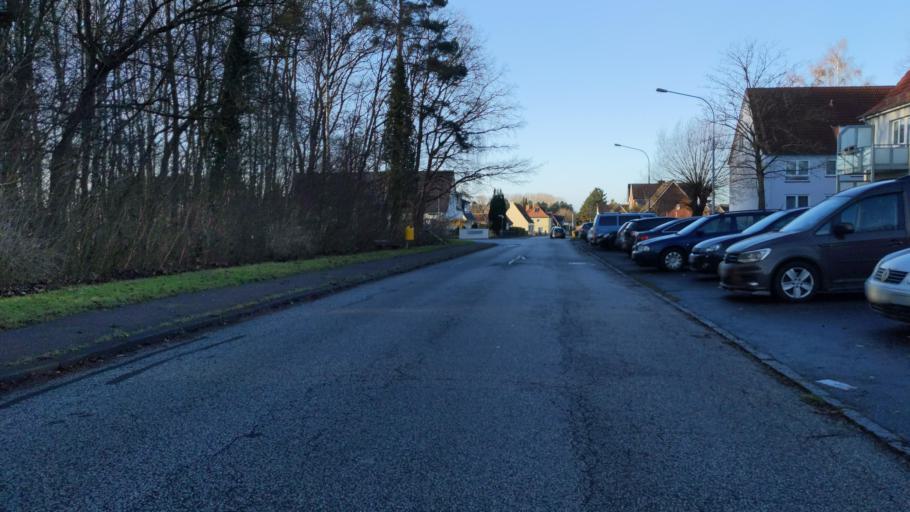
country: DE
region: Mecklenburg-Vorpommern
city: Selmsdorf
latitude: 53.9027
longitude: 10.8018
